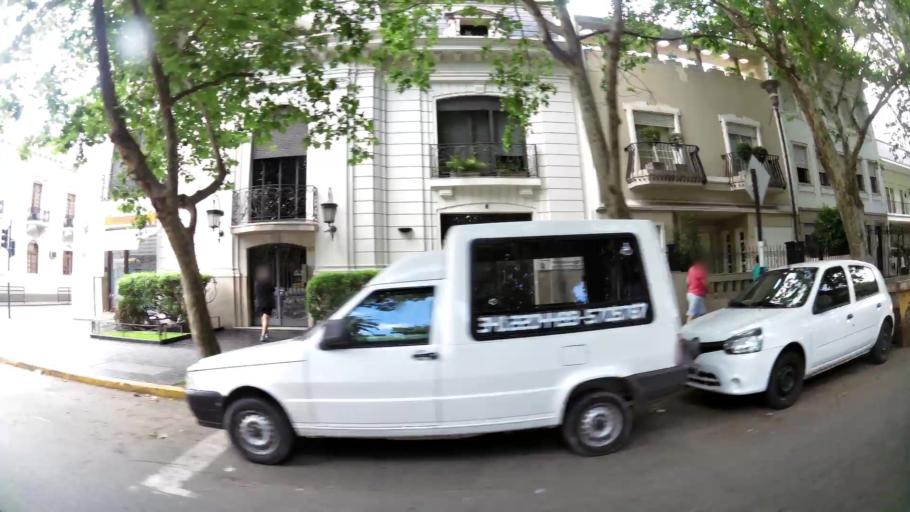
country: AR
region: Santa Fe
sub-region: Departamento de Rosario
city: Rosario
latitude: -32.9466
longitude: -60.6539
